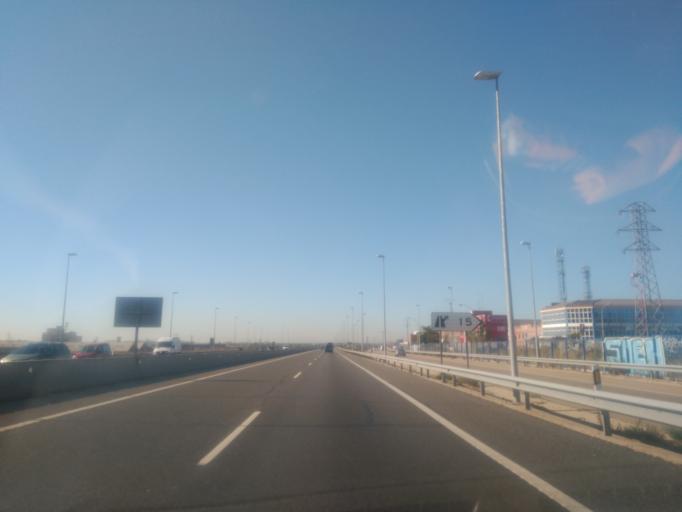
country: ES
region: Castille and Leon
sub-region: Provincia de Valladolid
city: Cisterniga
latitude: 41.6163
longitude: -4.7046
